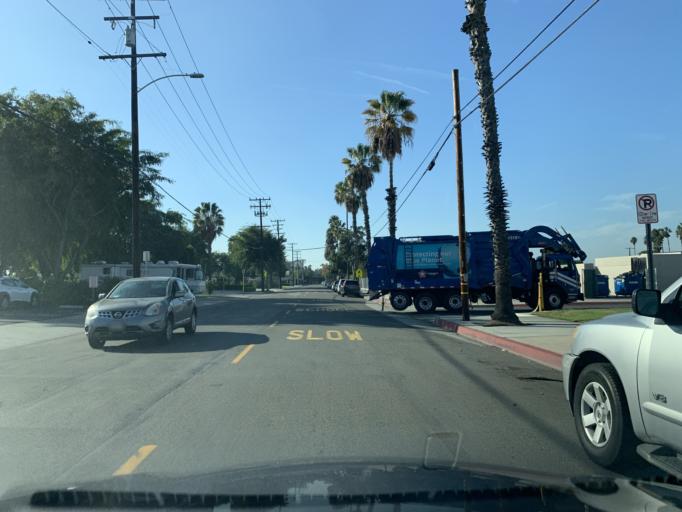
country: US
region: California
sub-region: Orange County
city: Anaheim
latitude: 33.8126
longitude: -117.9078
